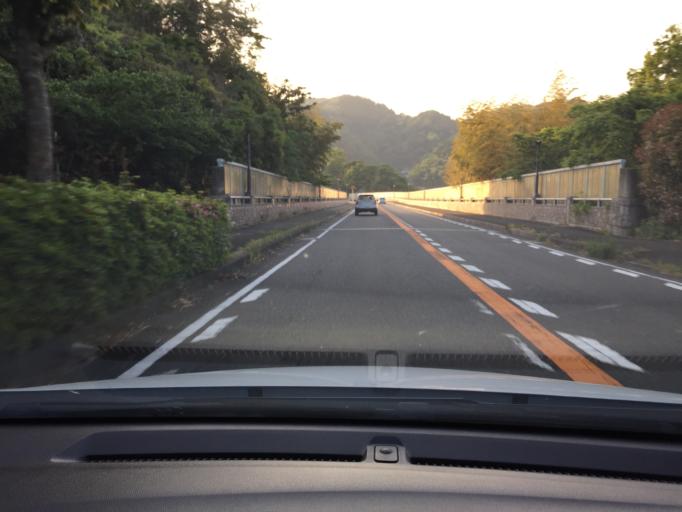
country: JP
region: Kanagawa
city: Hayama
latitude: 35.2651
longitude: 139.6097
